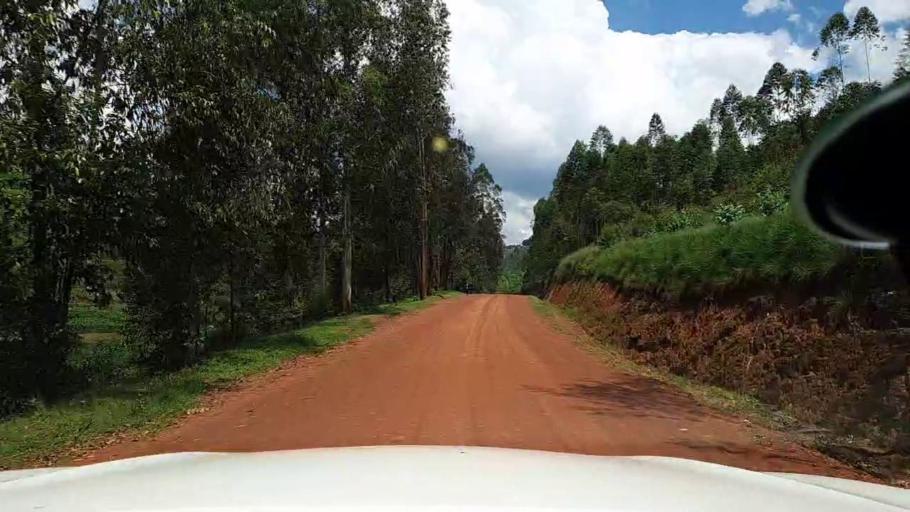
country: RW
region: Northern Province
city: Byumba
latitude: -1.6933
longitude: 29.8264
